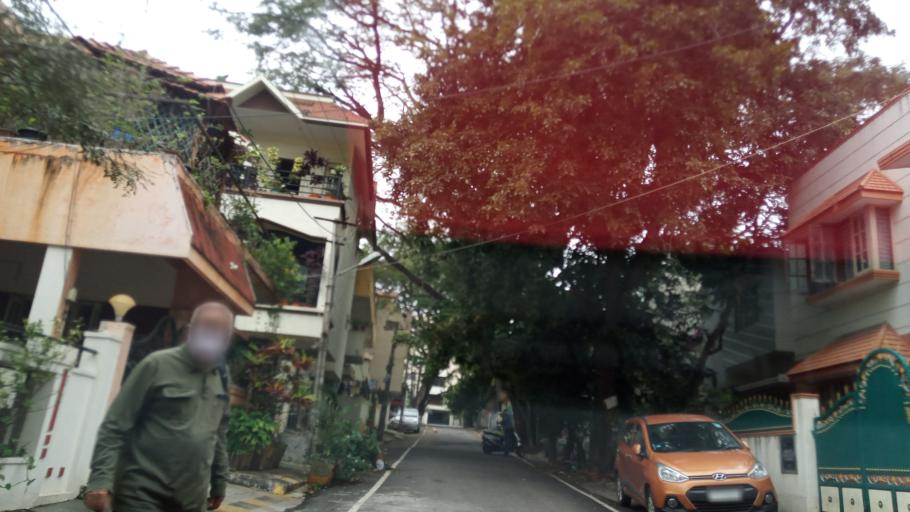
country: IN
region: Karnataka
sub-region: Bangalore Urban
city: Bangalore
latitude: 12.9389
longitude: 77.5401
